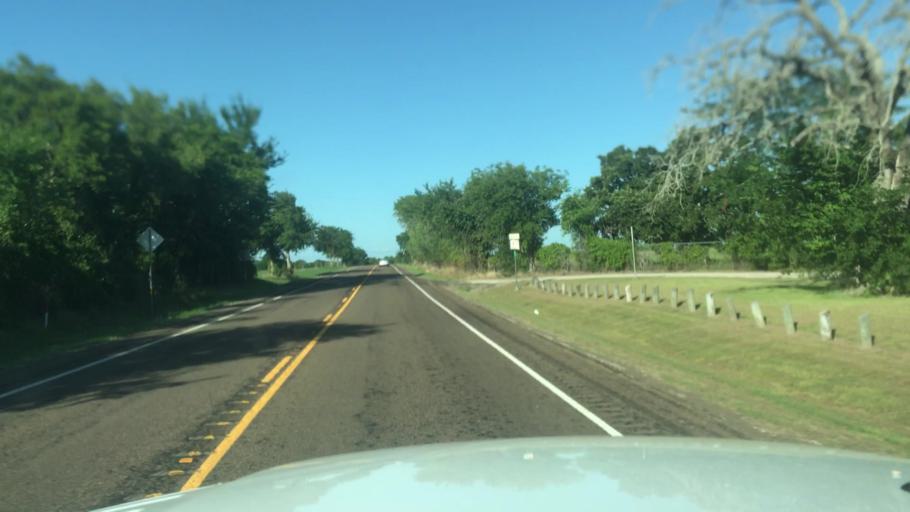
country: US
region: Texas
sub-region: Grimes County
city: Anderson
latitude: 30.6299
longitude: -95.8768
